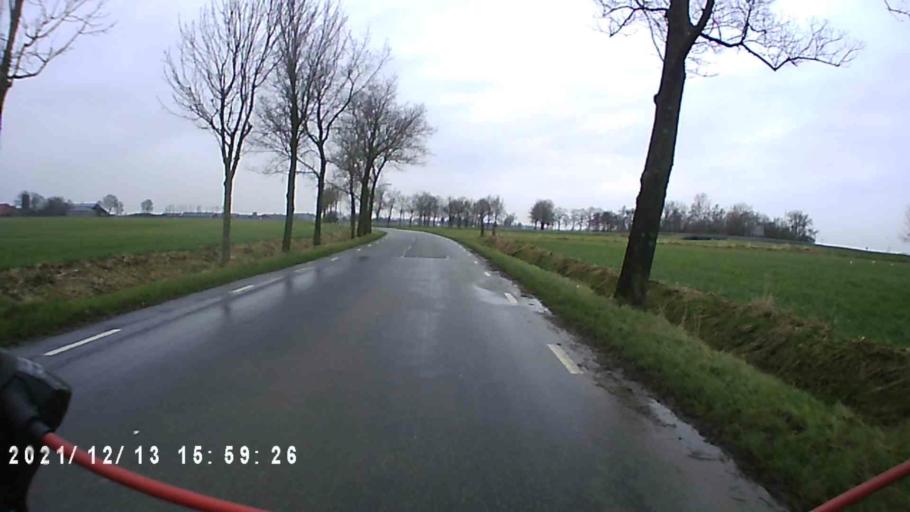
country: NL
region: Groningen
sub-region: Gemeente Appingedam
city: Appingedam
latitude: 53.3378
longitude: 6.8648
